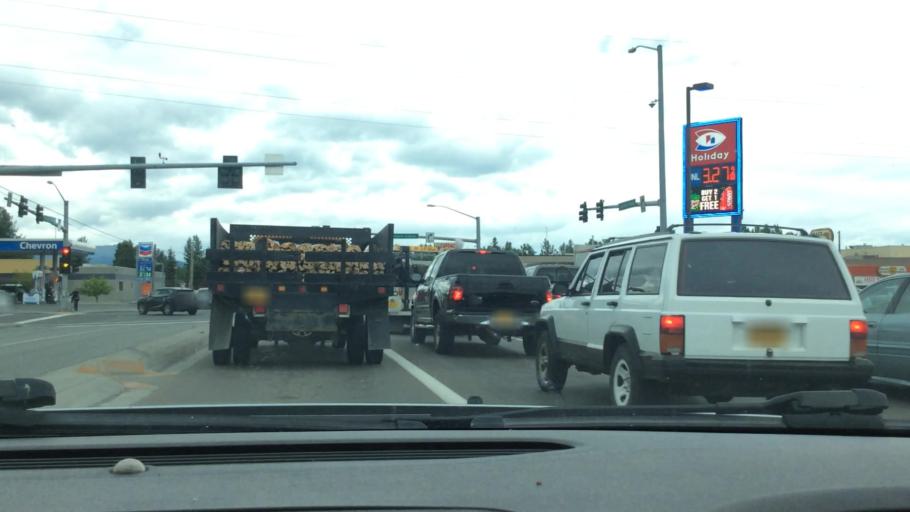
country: US
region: Alaska
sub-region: Anchorage Municipality
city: Anchorage
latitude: 61.1958
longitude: -149.7784
